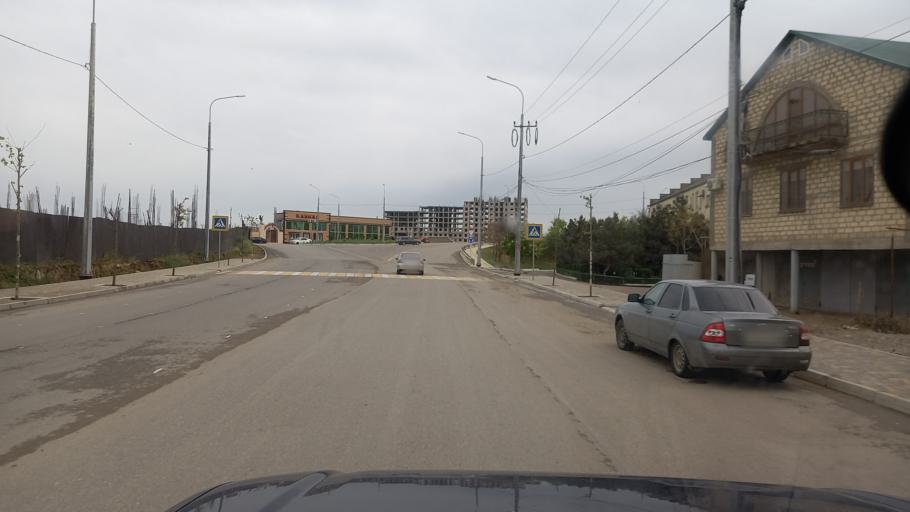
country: RU
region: Dagestan
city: Derbent
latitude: 42.0734
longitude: 48.2995
